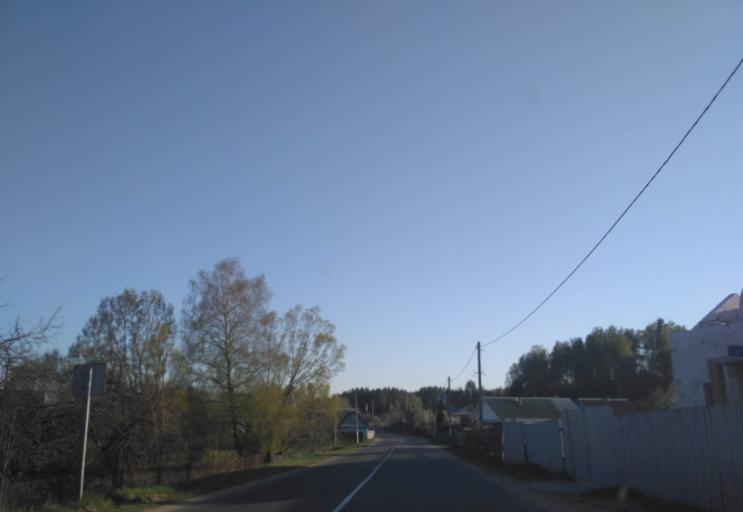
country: BY
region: Minsk
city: Radashkovichy
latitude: 54.1335
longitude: 27.2037
